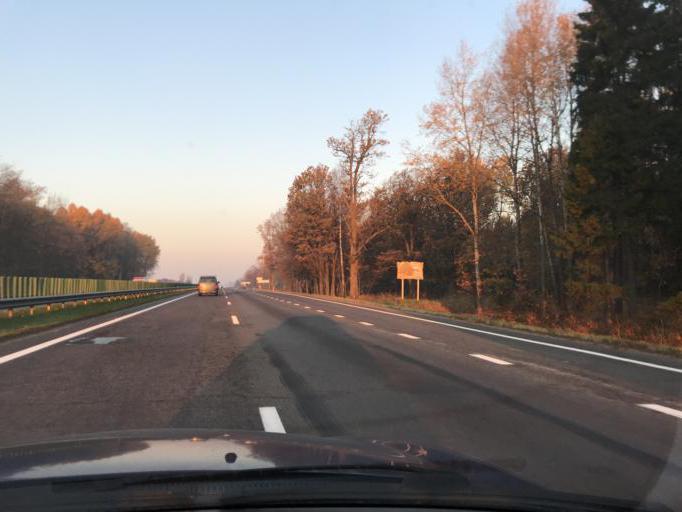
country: BY
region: Minsk
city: Novosel'ye
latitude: 53.9172
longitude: 27.2134
